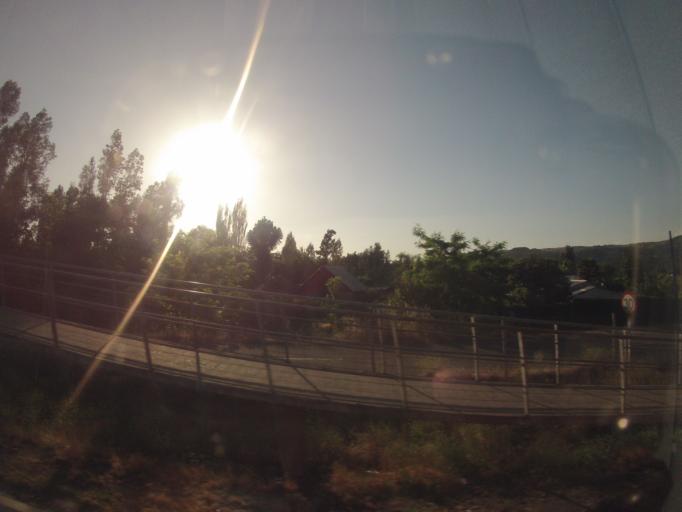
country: CL
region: O'Higgins
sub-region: Provincia de Colchagua
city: Chimbarongo
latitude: -34.6588
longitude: -70.9931
